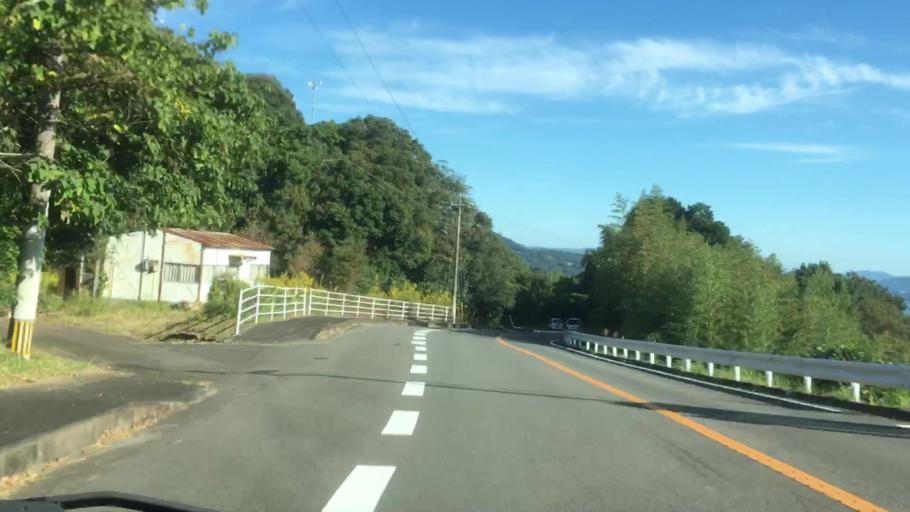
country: JP
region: Nagasaki
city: Sasebo
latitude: 32.9918
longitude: 129.7244
